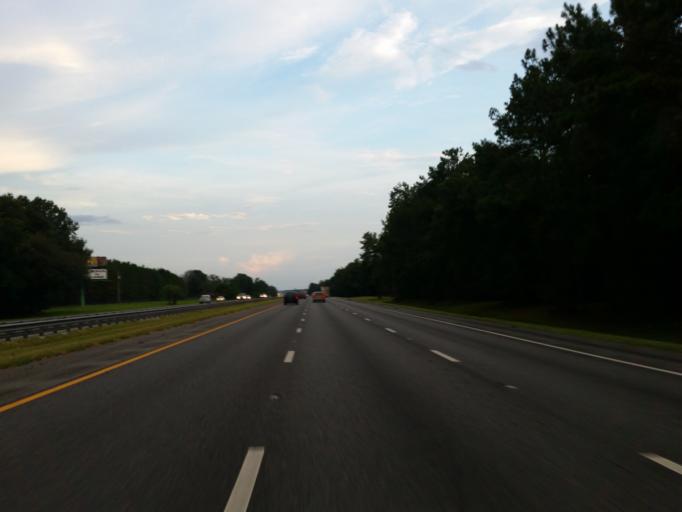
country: US
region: Florida
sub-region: Columbia County
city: Lake City
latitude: 30.1400
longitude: -82.6684
